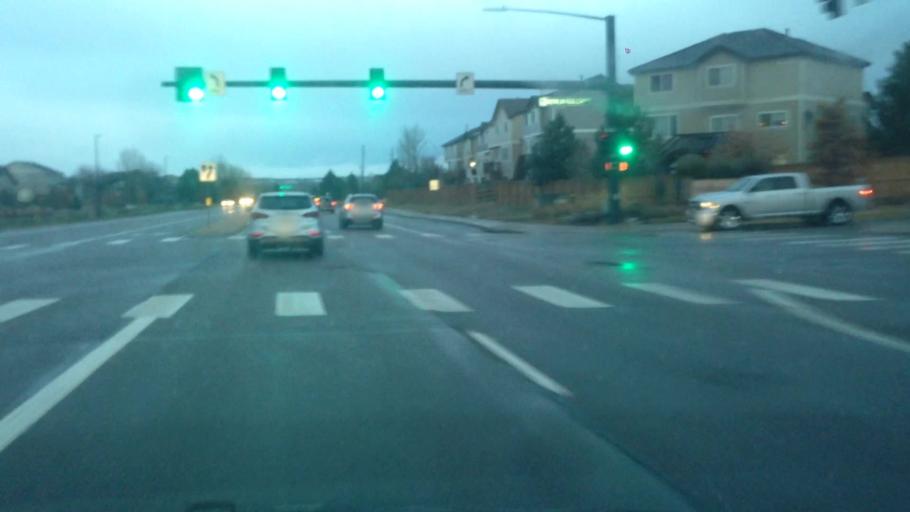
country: US
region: Colorado
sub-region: Douglas County
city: Stonegate
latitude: 39.5148
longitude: -104.8054
